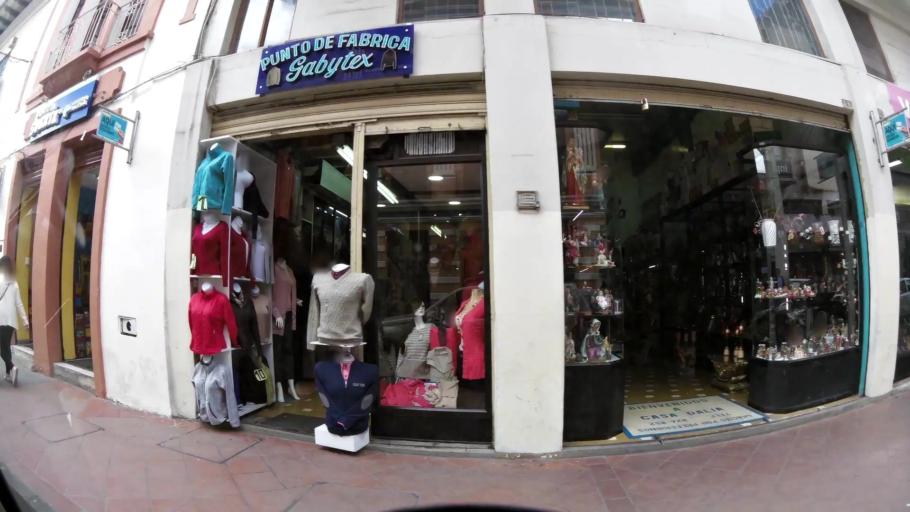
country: EC
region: Azuay
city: Cuenca
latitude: -2.8953
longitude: -79.0036
